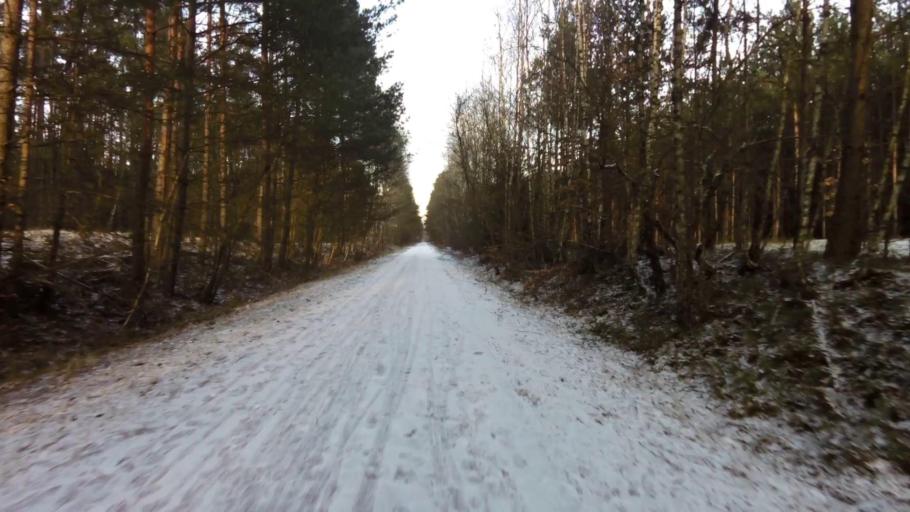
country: PL
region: West Pomeranian Voivodeship
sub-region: Powiat drawski
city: Zlocieniec
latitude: 53.5580
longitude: 16.0287
